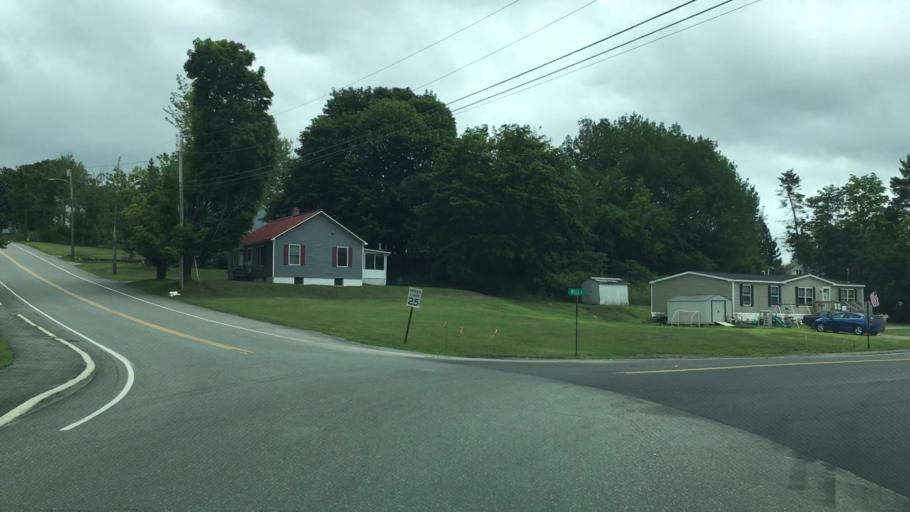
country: US
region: Maine
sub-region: Penobscot County
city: Bangor
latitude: 44.7667
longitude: -68.7797
